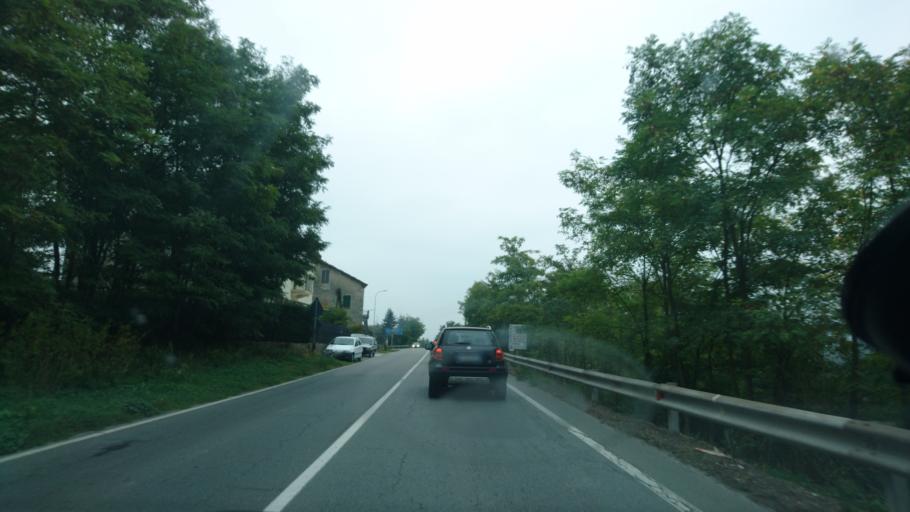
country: IT
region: Piedmont
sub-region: Provincia di Alessandria
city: Terzo
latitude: 44.6756
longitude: 8.4362
